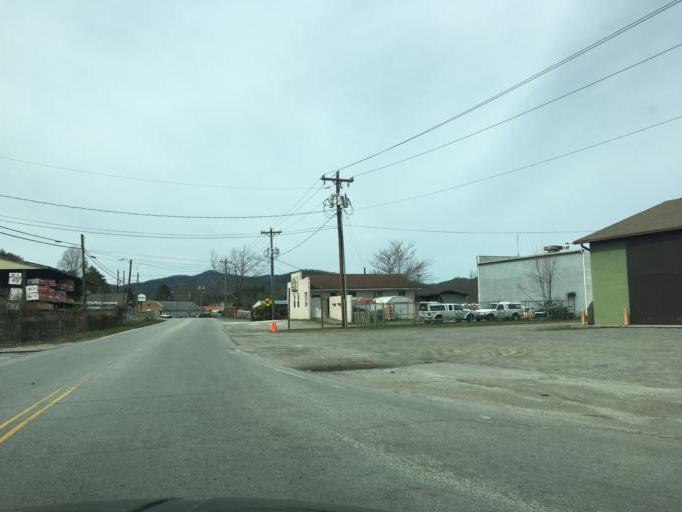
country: US
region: North Carolina
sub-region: Transylvania County
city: Brevard
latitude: 35.2540
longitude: -82.7003
